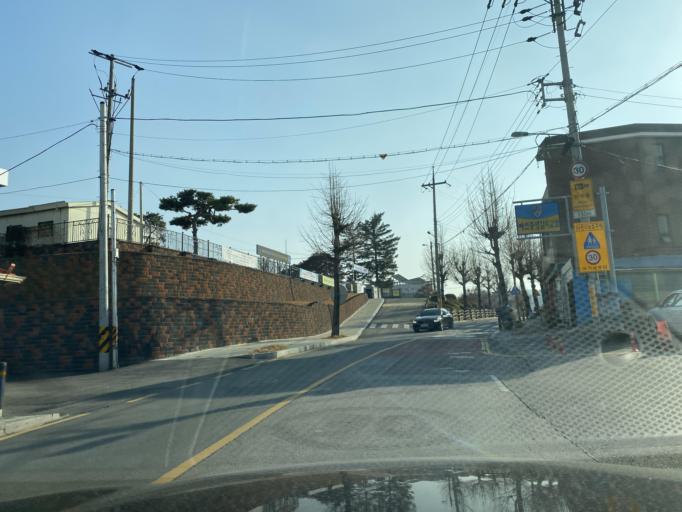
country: KR
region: Chungcheongnam-do
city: Yesan
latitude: 36.6854
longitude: 126.8327
